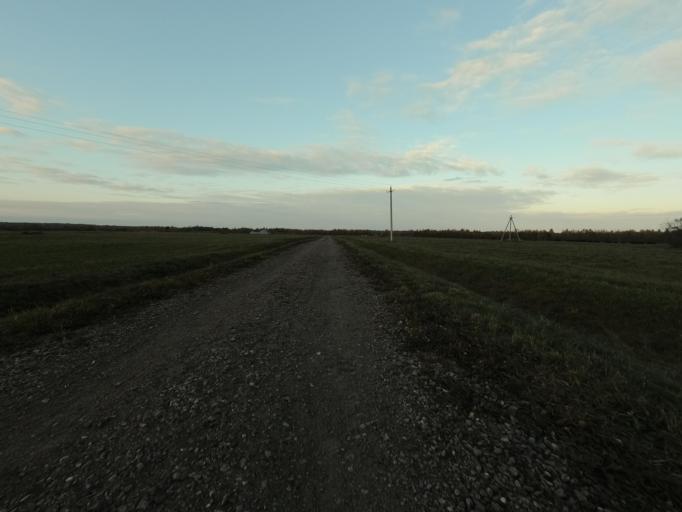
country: RU
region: Leningrad
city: Mga
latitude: 59.7860
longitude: 31.1985
